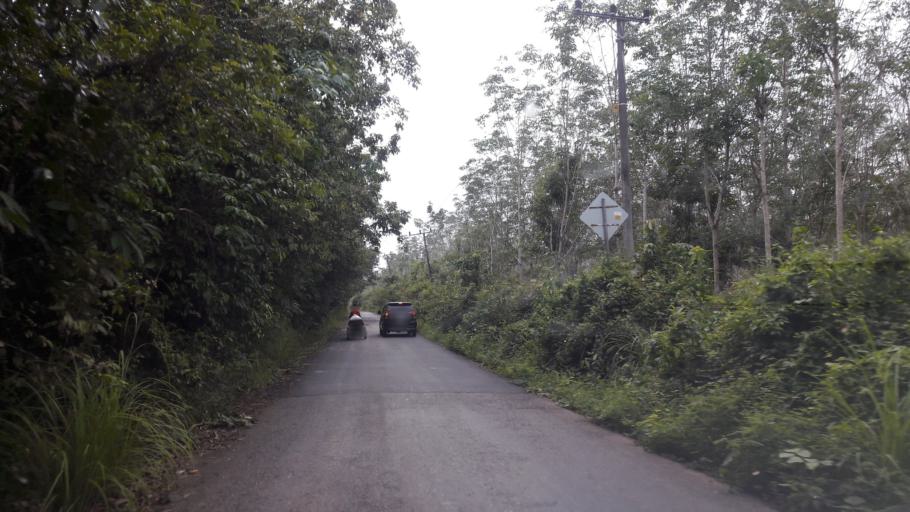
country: ID
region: South Sumatra
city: Gunungmenang
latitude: -3.1278
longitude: 104.1111
